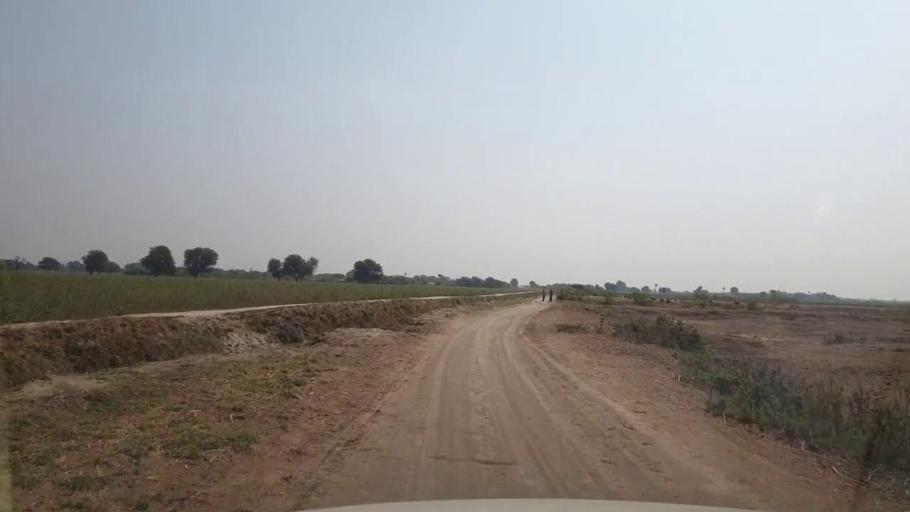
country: PK
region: Sindh
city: Chor
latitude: 25.4511
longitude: 69.6941
